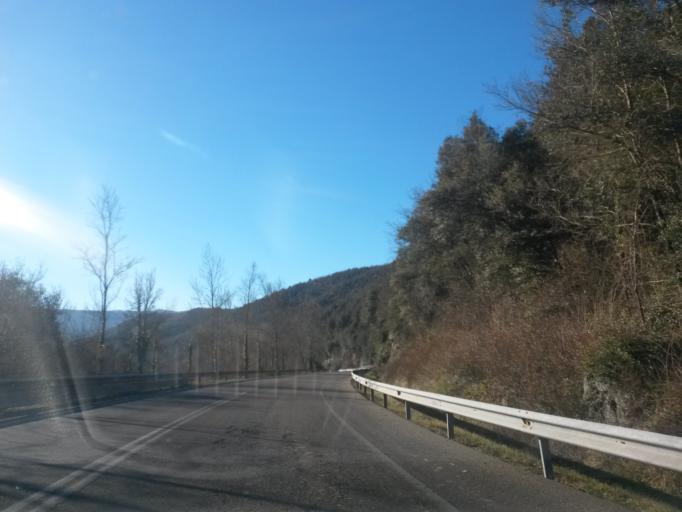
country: ES
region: Catalonia
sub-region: Provincia de Girona
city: Bas
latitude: 42.1176
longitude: 2.4906
